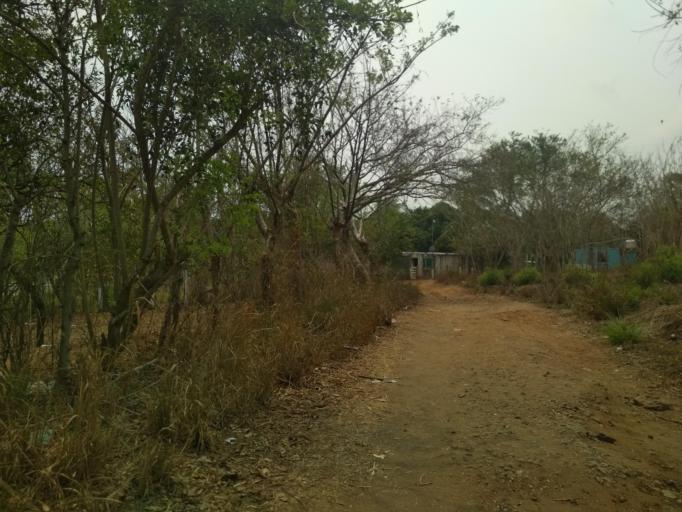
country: MX
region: Veracruz
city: Paso del Toro
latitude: 19.0246
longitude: -96.1384
